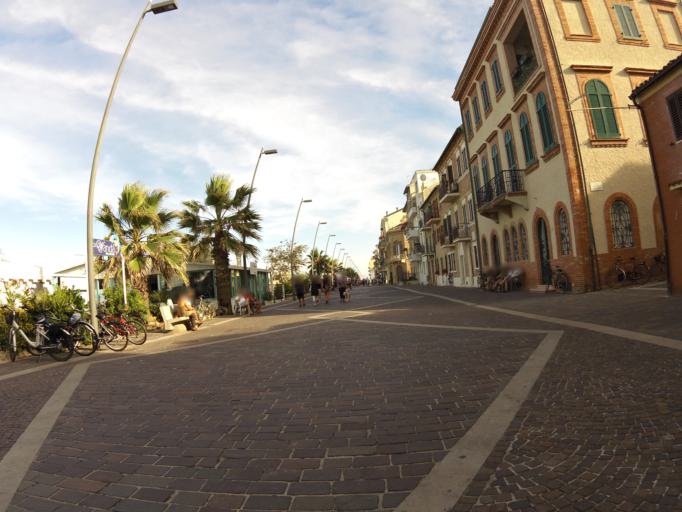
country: IT
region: The Marches
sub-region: Provincia di Macerata
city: Porto Recanati
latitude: 43.4339
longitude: 13.6649
